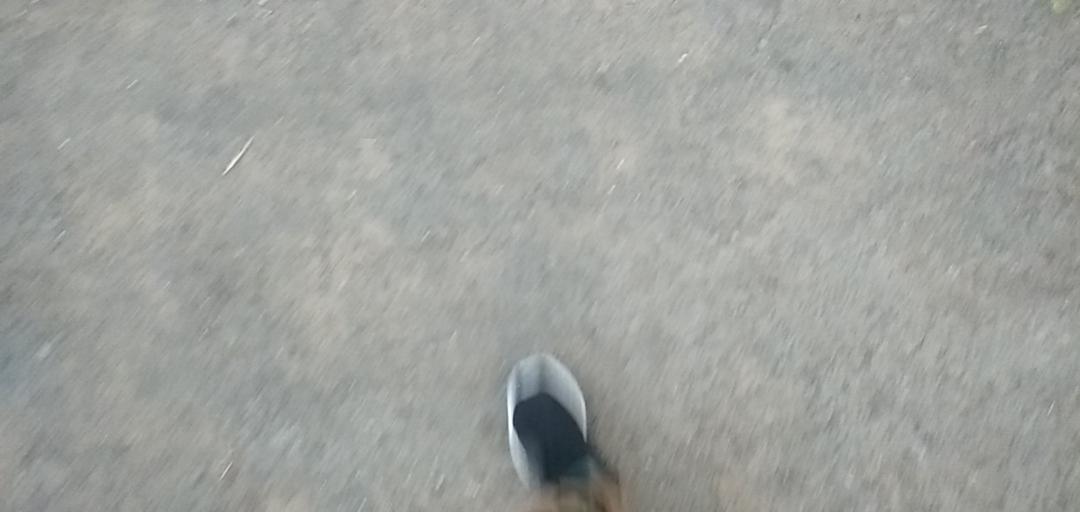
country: IN
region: Rajasthan
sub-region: Kota
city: Kota
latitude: 25.2219
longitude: 75.8823
